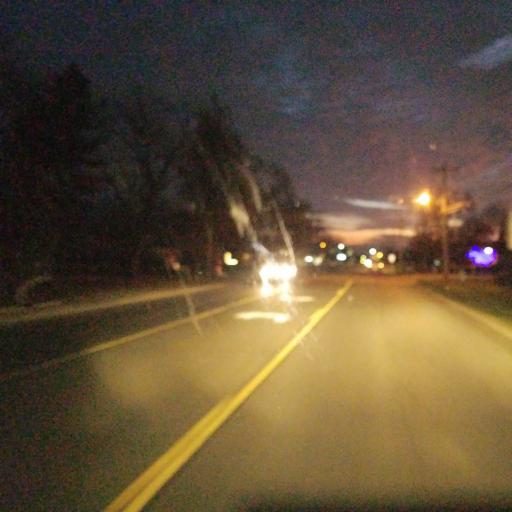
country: US
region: Illinois
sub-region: Peoria County
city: Hanna City
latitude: 40.6916
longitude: -89.7916
